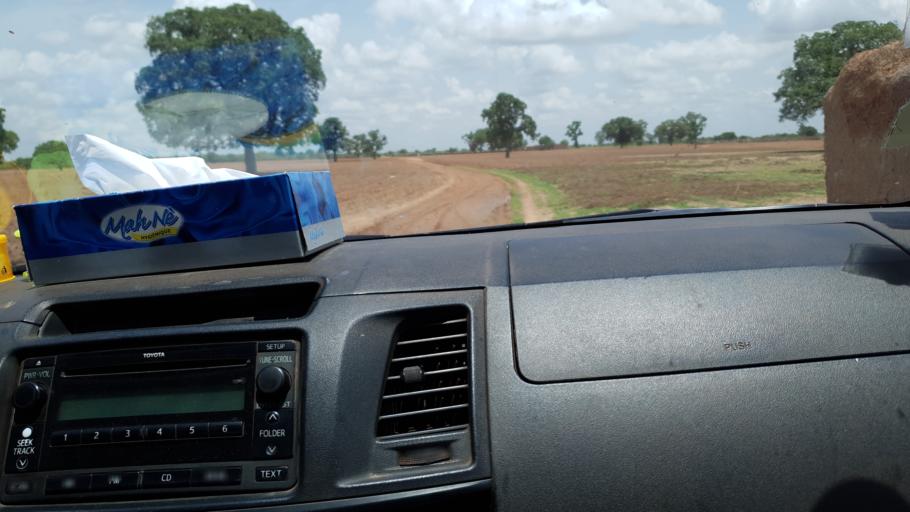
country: ML
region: Koulikoro
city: Banamba
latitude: 13.3795
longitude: -7.2006
